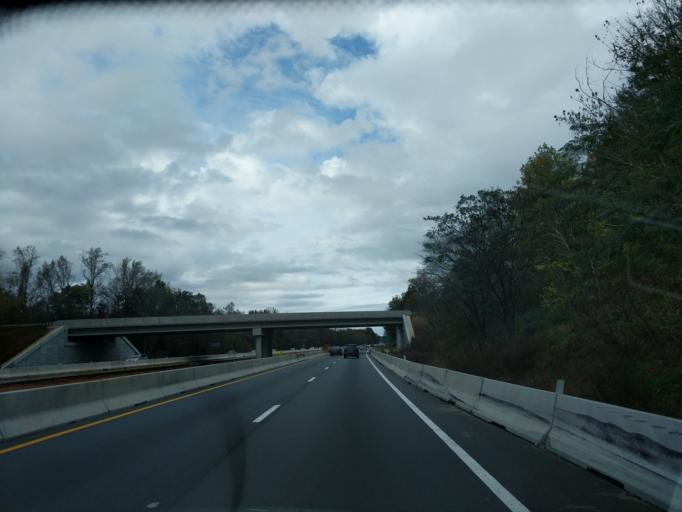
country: US
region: North Carolina
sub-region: Rowan County
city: China Grove
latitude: 35.5593
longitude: -80.5677
